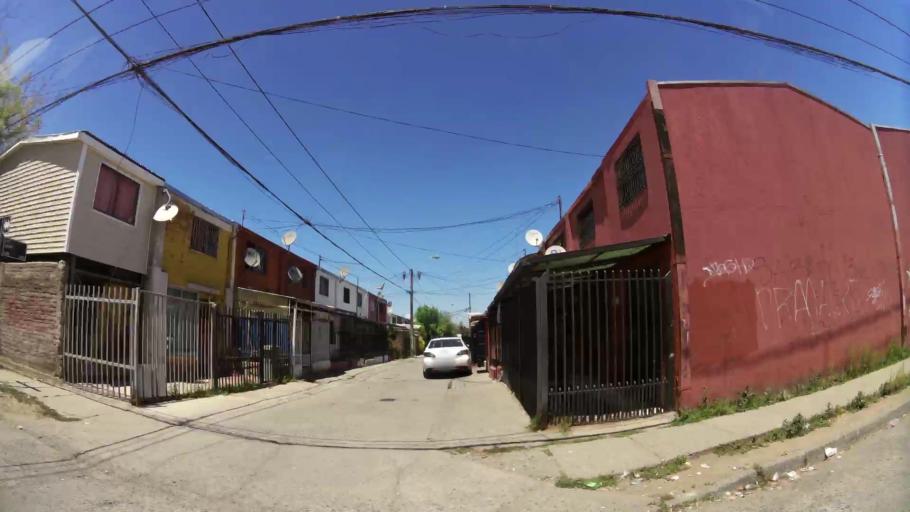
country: CL
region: Santiago Metropolitan
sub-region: Provincia de Santiago
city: La Pintana
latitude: -33.5736
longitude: -70.6683
